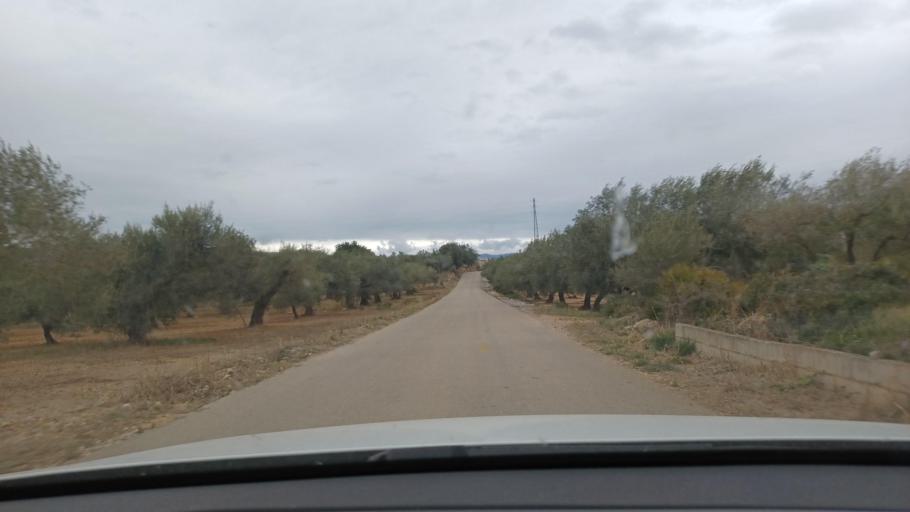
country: ES
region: Valencia
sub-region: Provincia de Castello
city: Traiguera
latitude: 40.5129
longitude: 0.2926
